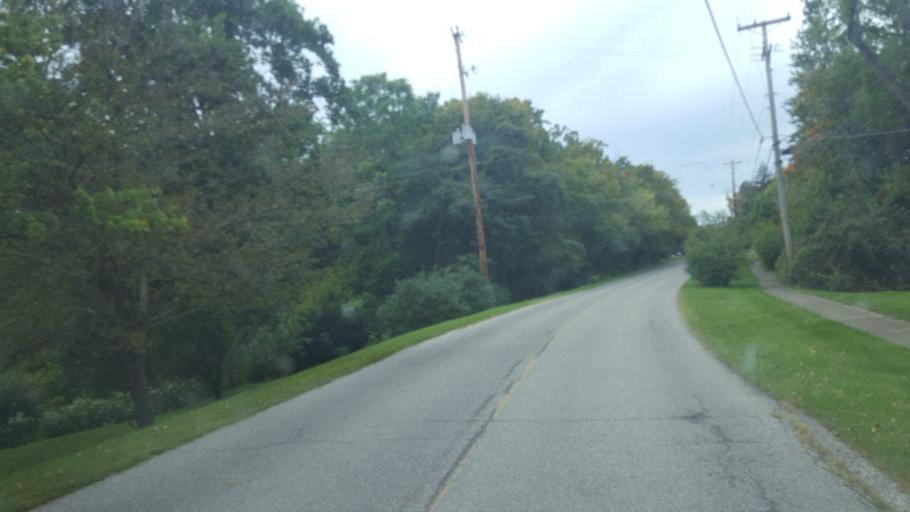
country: US
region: Ohio
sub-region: Delaware County
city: Sunbury
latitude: 40.2485
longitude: -82.8485
